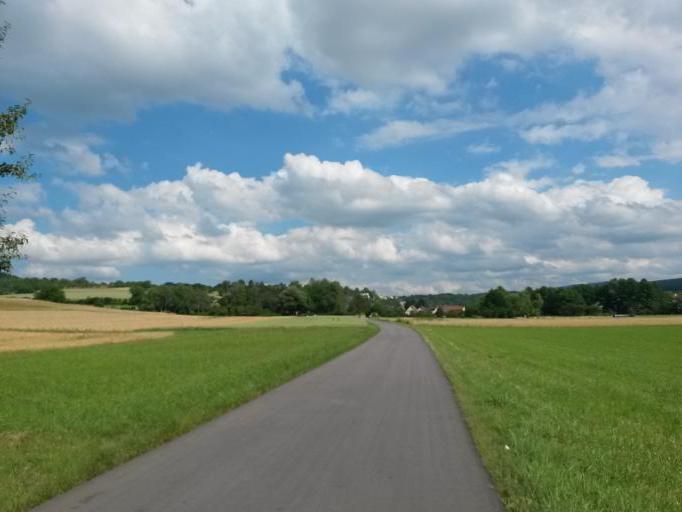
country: DE
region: Baden-Wuerttemberg
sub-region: Karlsruhe Region
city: Neuenburg
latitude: 48.9073
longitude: 8.5681
